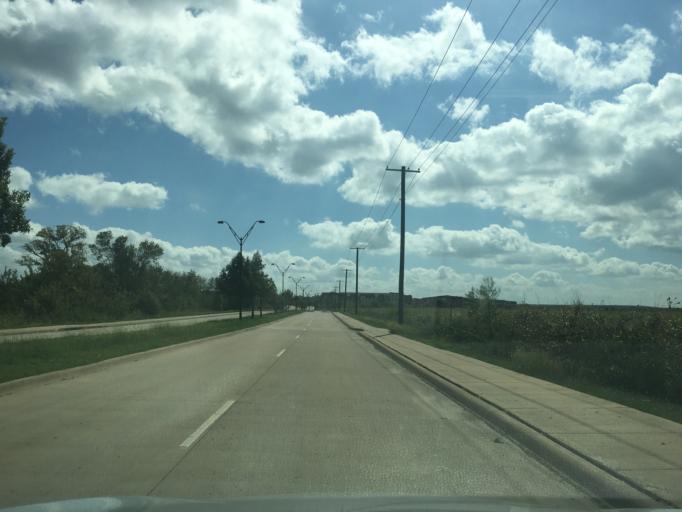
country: US
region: Texas
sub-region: Dallas County
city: Sachse
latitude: 32.9569
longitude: -96.5925
